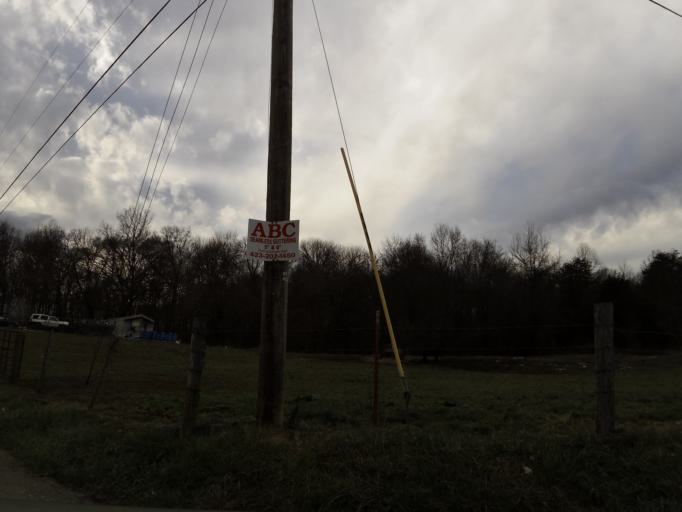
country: US
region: Tennessee
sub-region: Greene County
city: Tusculum
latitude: 36.2091
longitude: -82.7483
